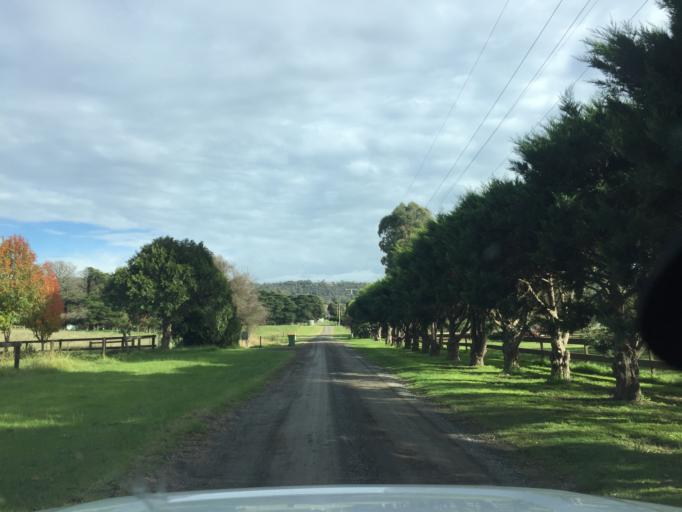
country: AU
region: Victoria
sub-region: Yarra Ranges
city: Yarra Glen
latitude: -37.6394
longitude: 145.3779
